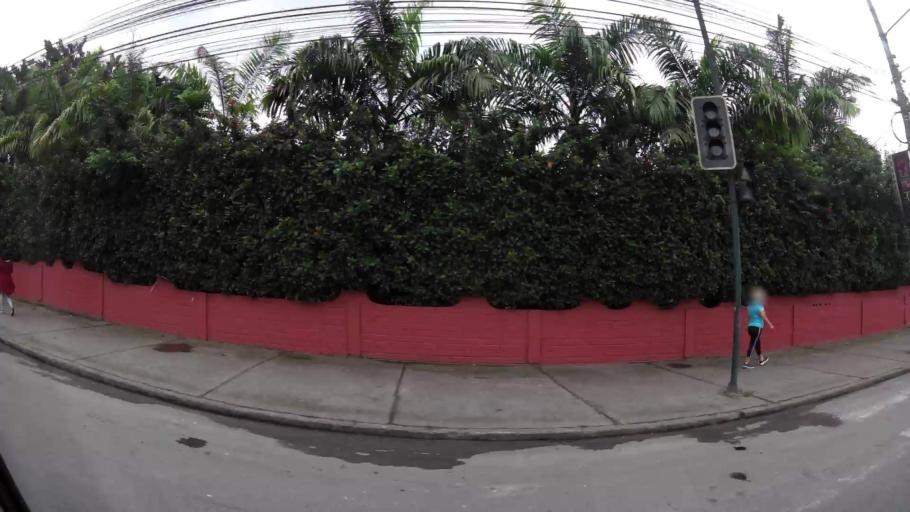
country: EC
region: Santo Domingo de los Tsachilas
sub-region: Canton Santo Domingo de los Colorados
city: Santo Domingo de los Colorados
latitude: -0.2479
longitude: -79.1552
